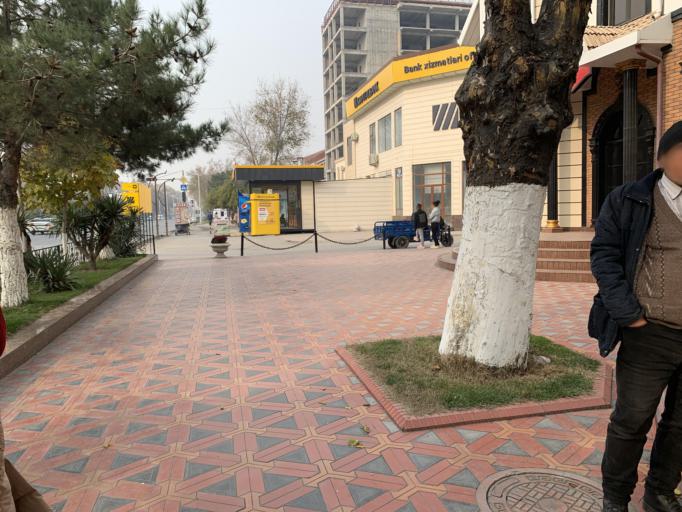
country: UZ
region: Fergana
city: Qo`qon
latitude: 40.5464
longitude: 70.9288
